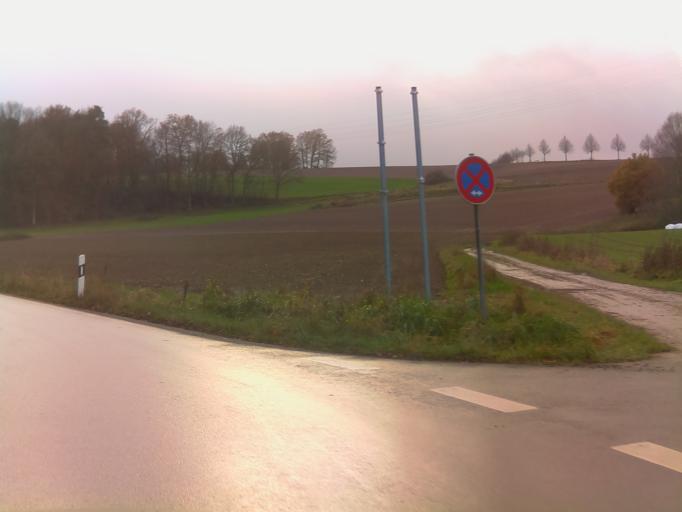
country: DE
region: Hesse
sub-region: Regierungsbezirk Kassel
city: Eichenzell
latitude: 50.5168
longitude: 9.6733
